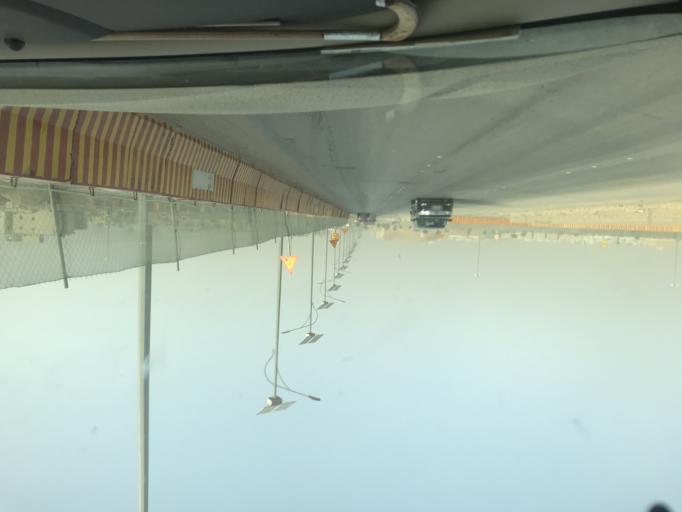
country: SA
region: Ar Riyad
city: Riyadh
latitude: 24.8446
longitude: 46.6647
